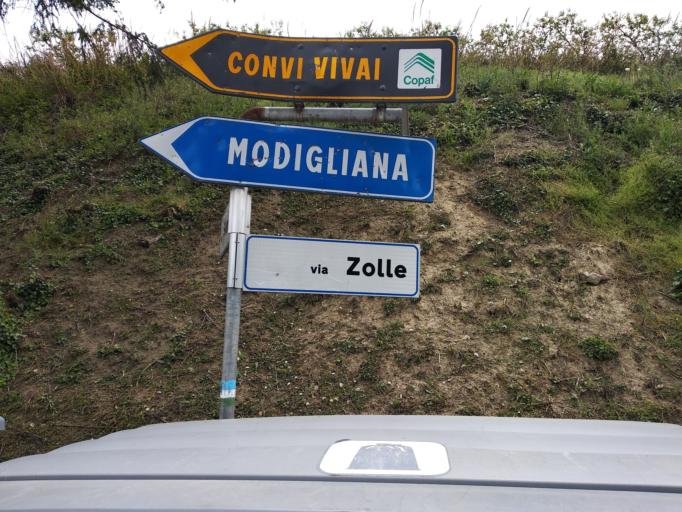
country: IT
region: Emilia-Romagna
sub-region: Provincia di Ravenna
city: Fognano
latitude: 44.2120
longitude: 11.7540
